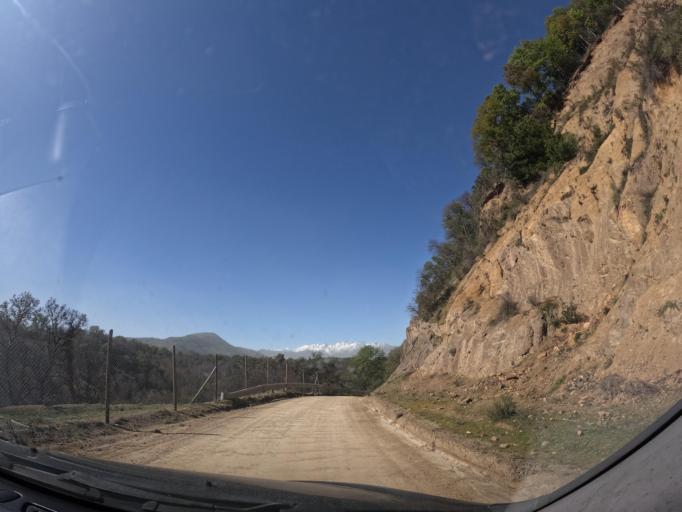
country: CL
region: Maule
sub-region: Provincia de Linares
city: Longavi
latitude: -36.2426
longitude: -71.4364
